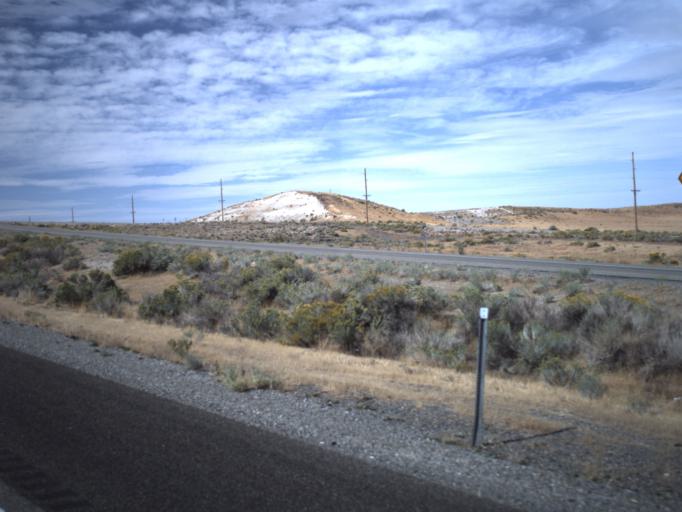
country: US
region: Utah
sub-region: Tooele County
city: Grantsville
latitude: 40.7706
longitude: -112.9816
